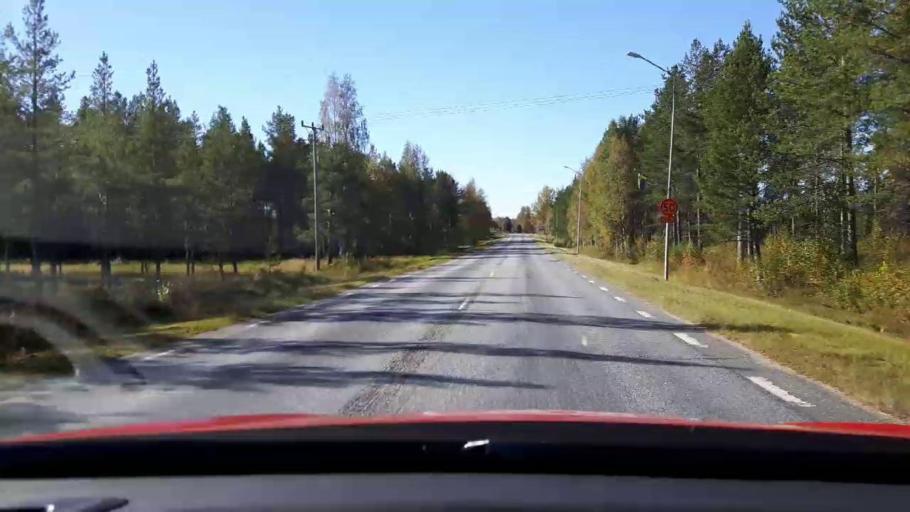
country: SE
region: Jaemtland
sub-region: Harjedalens Kommun
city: Sveg
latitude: 62.3173
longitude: 14.0515
